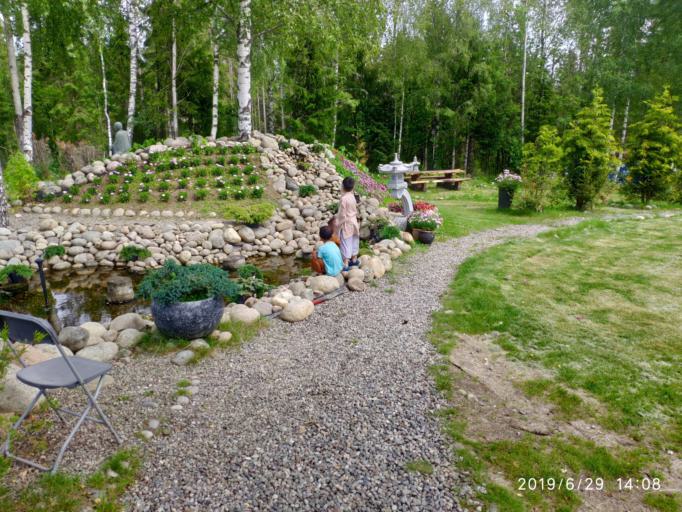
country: NO
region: Akershus
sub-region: Ullensaker
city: Jessheim
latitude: 60.1732
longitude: 11.1703
